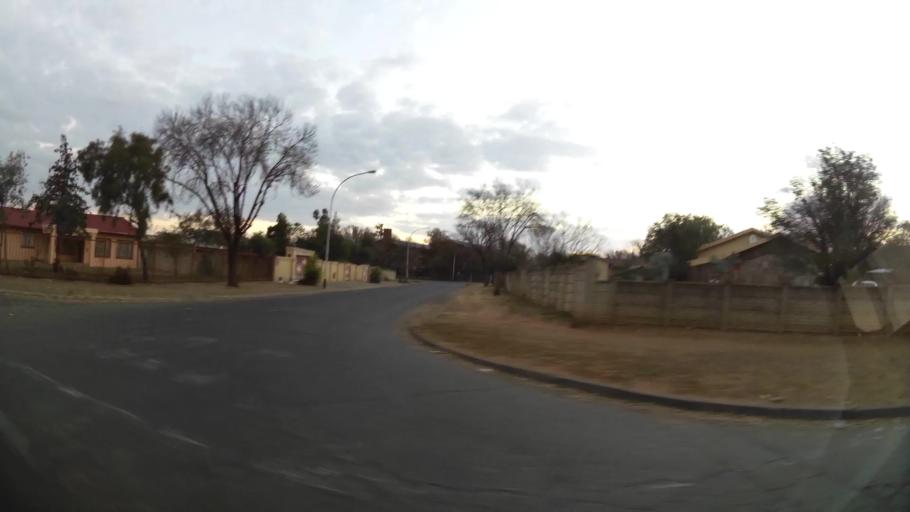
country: ZA
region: Orange Free State
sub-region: Mangaung Metropolitan Municipality
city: Bloemfontein
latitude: -29.1684
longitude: 26.1925
